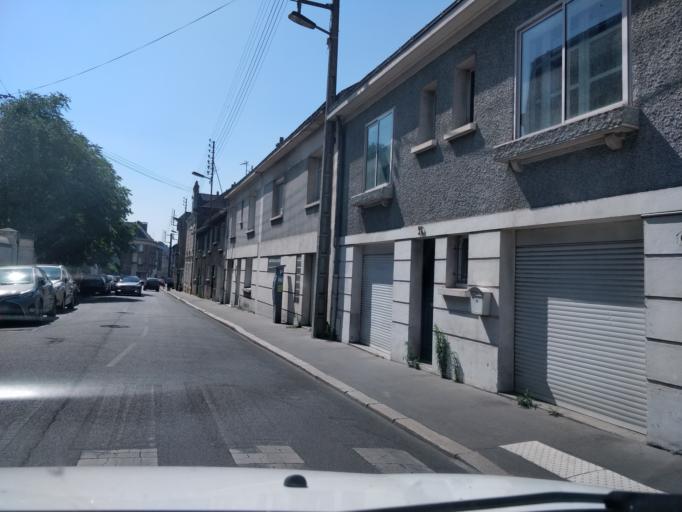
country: FR
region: Pays de la Loire
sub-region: Departement de la Loire-Atlantique
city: Nantes
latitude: 47.2247
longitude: -1.5393
